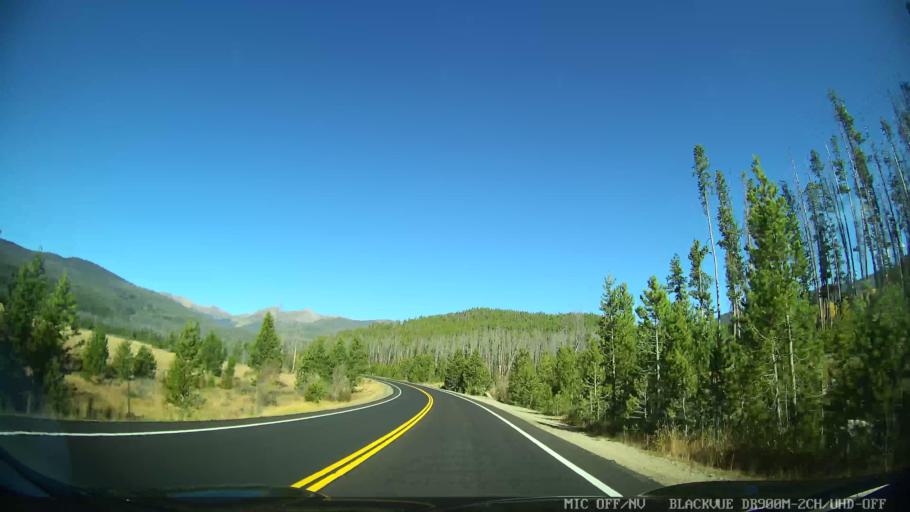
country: US
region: Colorado
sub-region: Grand County
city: Granby
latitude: 40.3174
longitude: -105.8449
